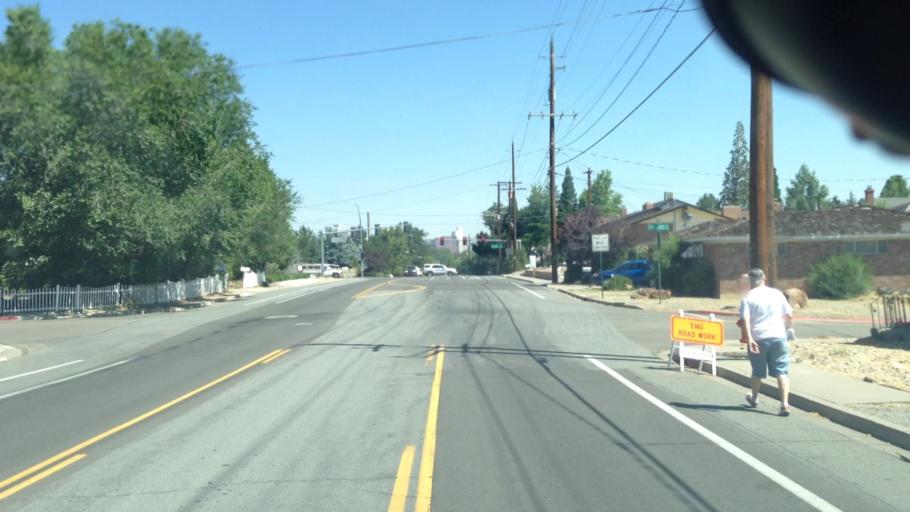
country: US
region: Nevada
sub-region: Washoe County
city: Reno
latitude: 39.5045
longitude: -119.8126
